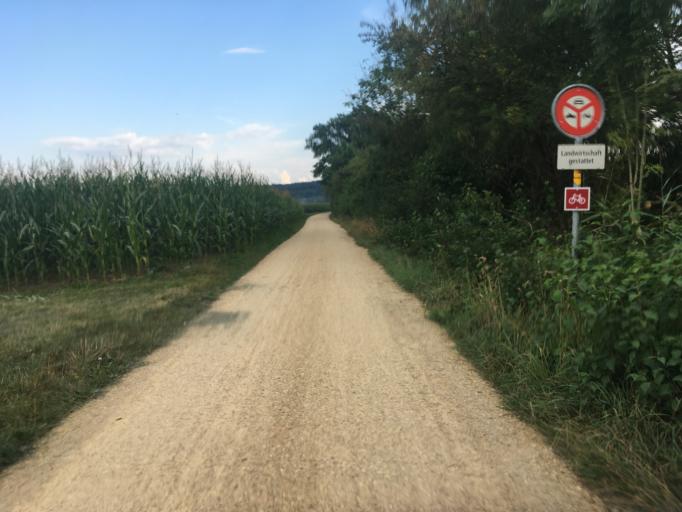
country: CH
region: Solothurn
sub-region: Bezirk Lebern
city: Langendorf
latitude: 47.2026
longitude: 7.4977
